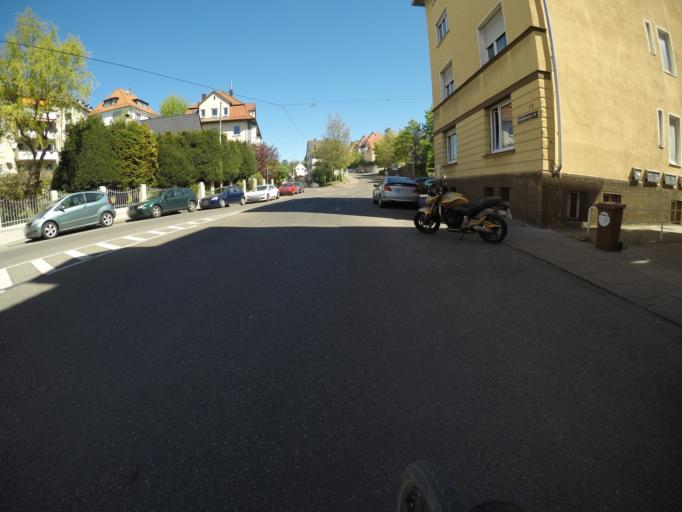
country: DE
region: Baden-Wuerttemberg
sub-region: Regierungsbezirk Stuttgart
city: Fellbach
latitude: 48.7829
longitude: 9.2567
